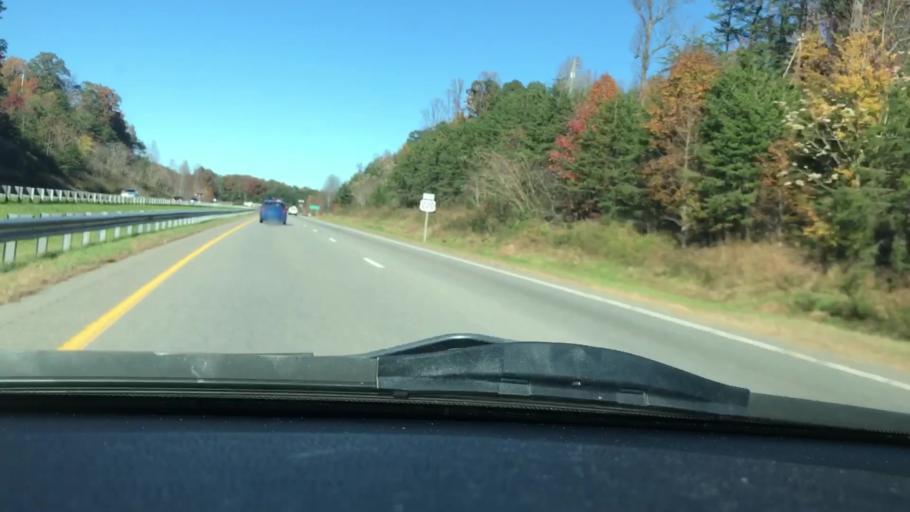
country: US
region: North Carolina
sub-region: Rockingham County
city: Stoneville
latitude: 36.4732
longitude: -79.9259
